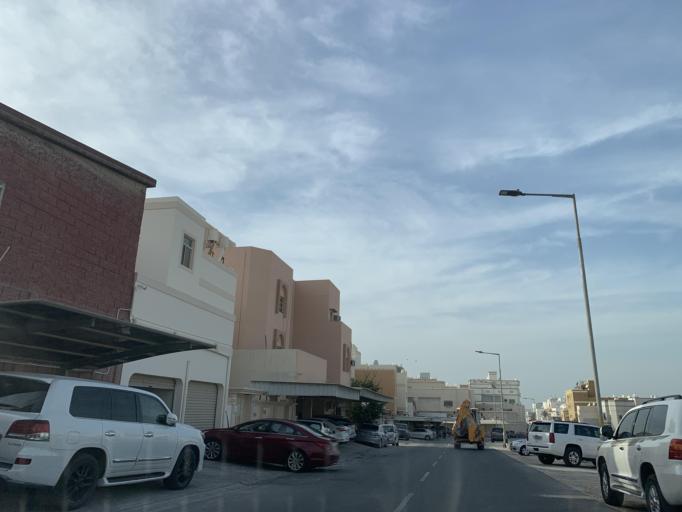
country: BH
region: Northern
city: Ar Rifa'
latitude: 26.1229
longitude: 50.5818
